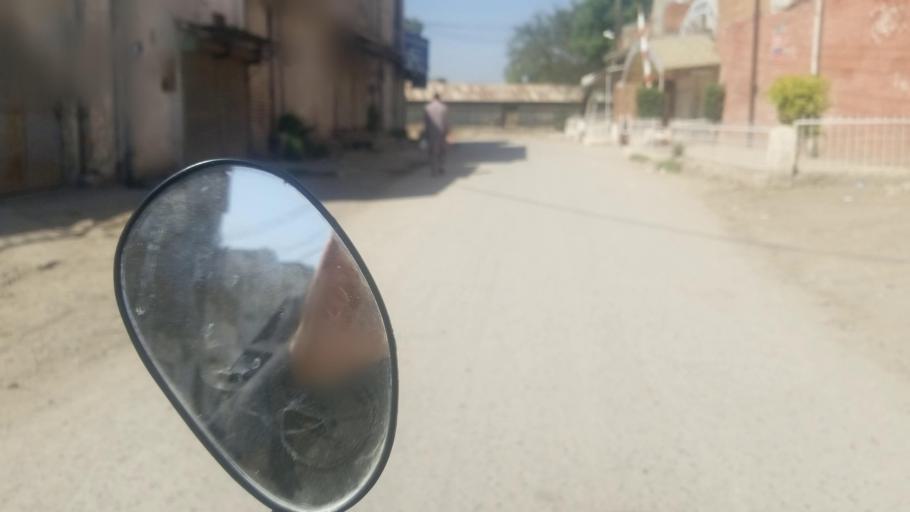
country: PK
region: Khyber Pakhtunkhwa
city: Peshawar
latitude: 34.0167
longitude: 71.5860
